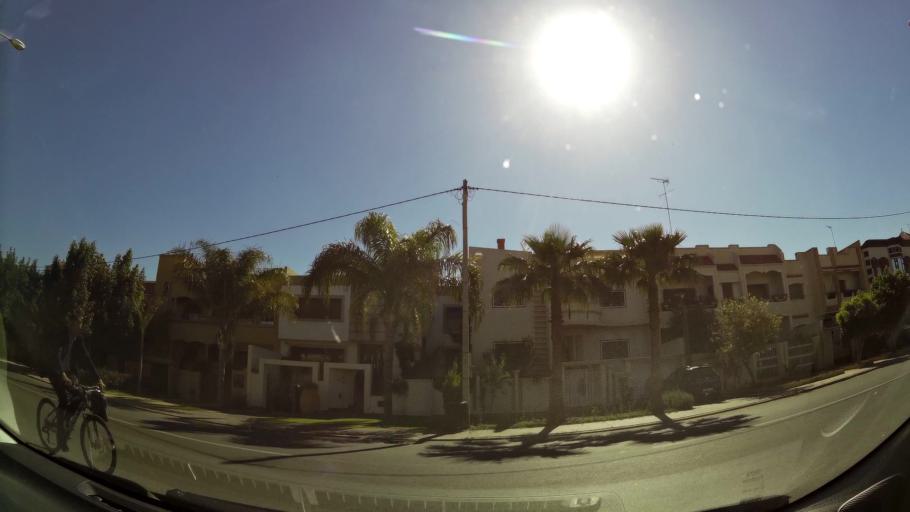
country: MA
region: Oriental
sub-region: Oujda-Angad
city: Oujda
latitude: 34.6634
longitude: -1.8955
